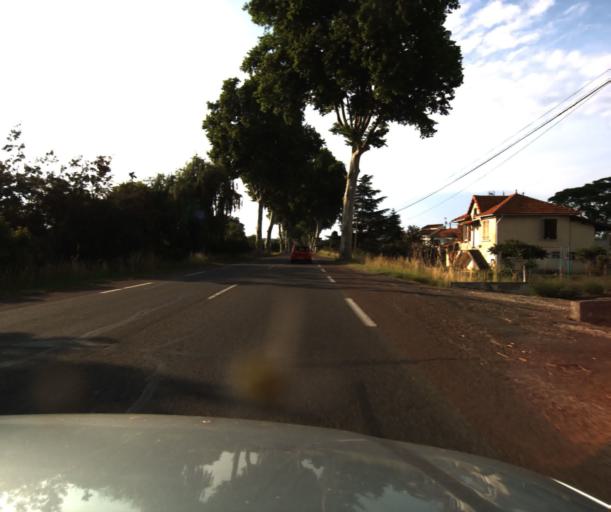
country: FR
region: Midi-Pyrenees
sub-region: Departement du Tarn-et-Garonne
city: Moissac
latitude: 44.0819
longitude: 1.0906
